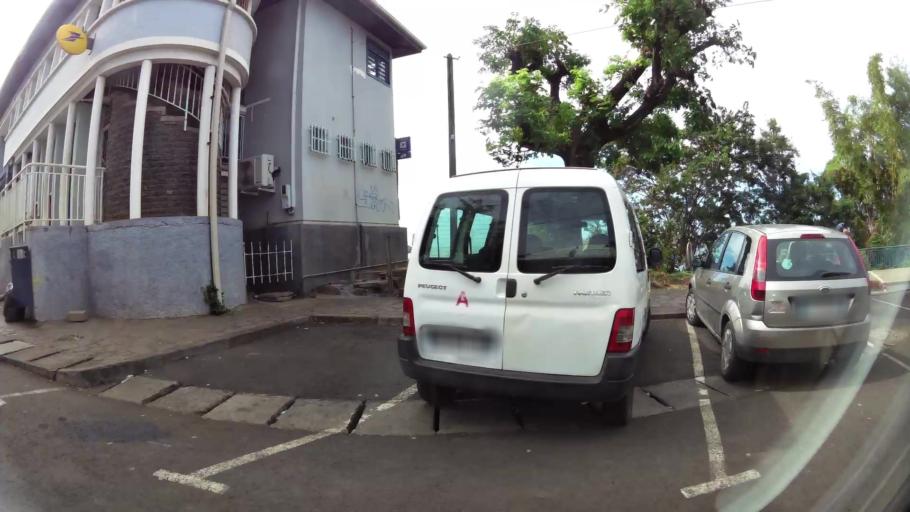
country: YT
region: Mamoudzou
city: Mamoudzou
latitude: -12.7798
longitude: 45.2321
